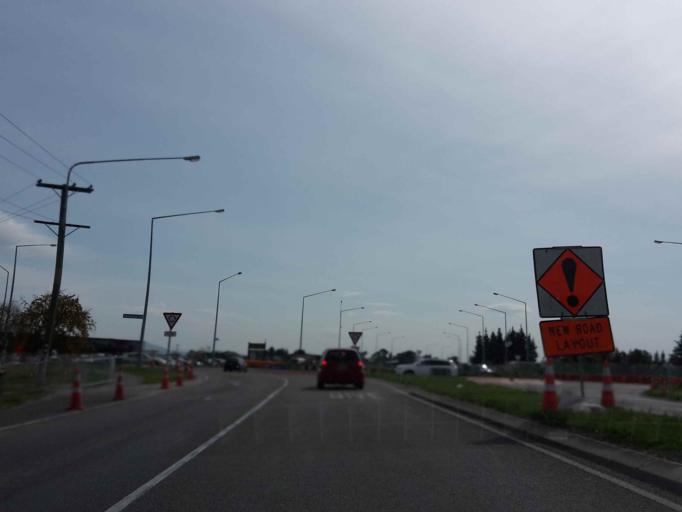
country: NZ
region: Canterbury
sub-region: Christchurch City
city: Christchurch
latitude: -43.4795
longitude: 172.5559
